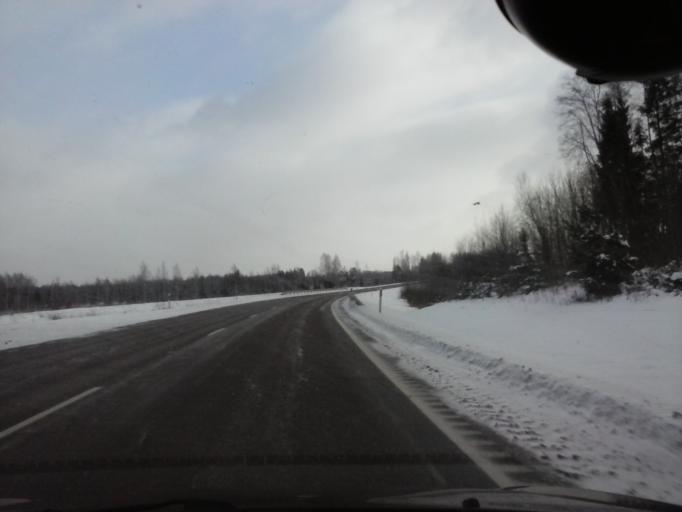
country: EE
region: Viljandimaa
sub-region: Viljandi linn
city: Viljandi
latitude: 58.3496
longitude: 25.4633
